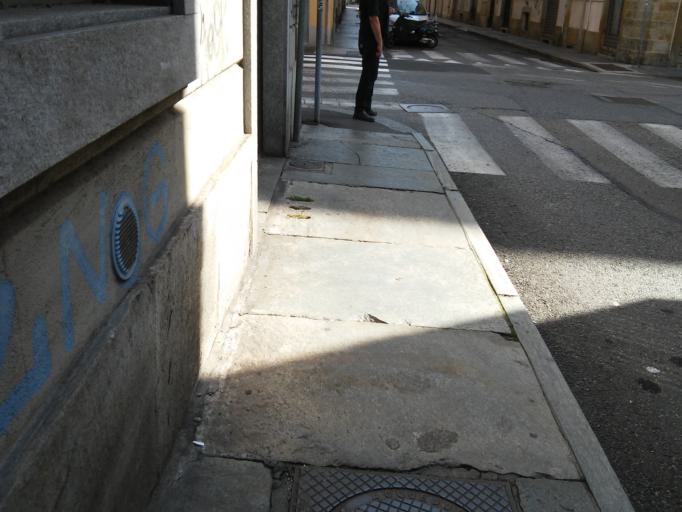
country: IT
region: Piedmont
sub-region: Provincia di Torino
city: Turin
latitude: 45.0765
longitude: 7.6771
